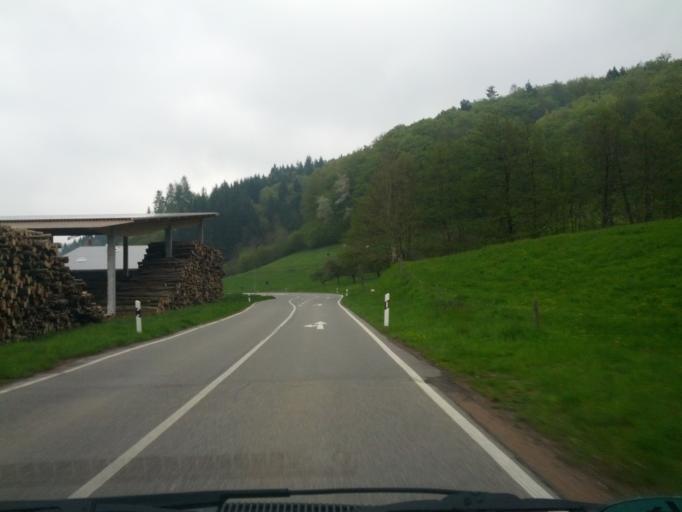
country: DE
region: Baden-Wuerttemberg
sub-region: Freiburg Region
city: Hausen
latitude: 47.7052
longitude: 7.7997
